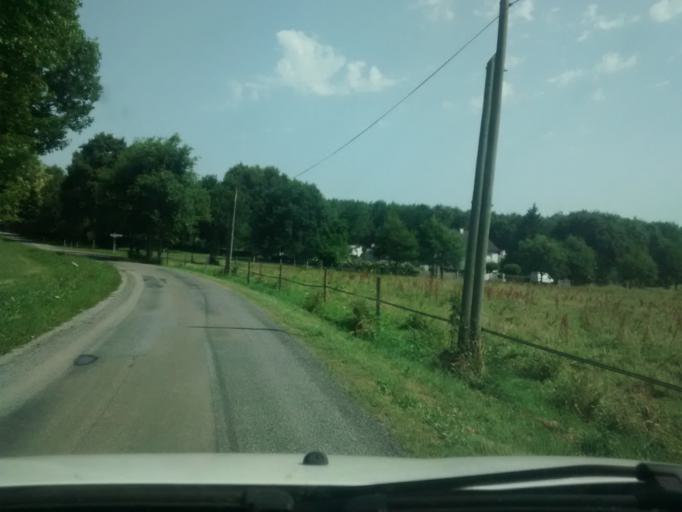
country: FR
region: Brittany
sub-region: Departement d'Ille-et-Vilaine
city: Cesson-Sevigne
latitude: 48.1386
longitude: -1.5941
